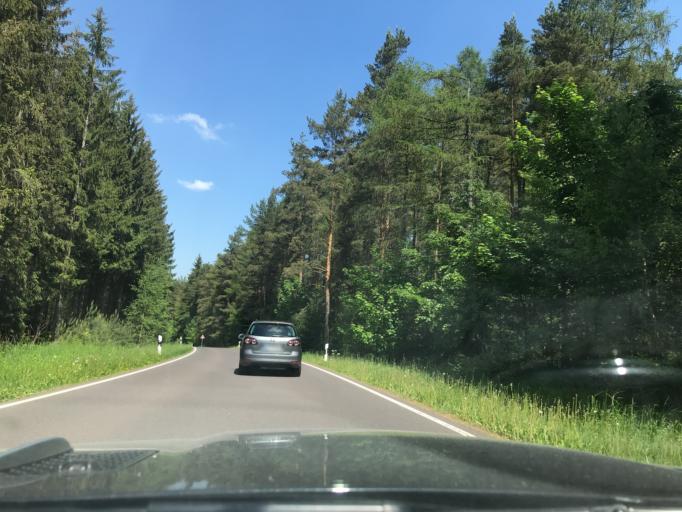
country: DE
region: Thuringia
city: Neuhaus
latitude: 50.7087
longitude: 10.9330
